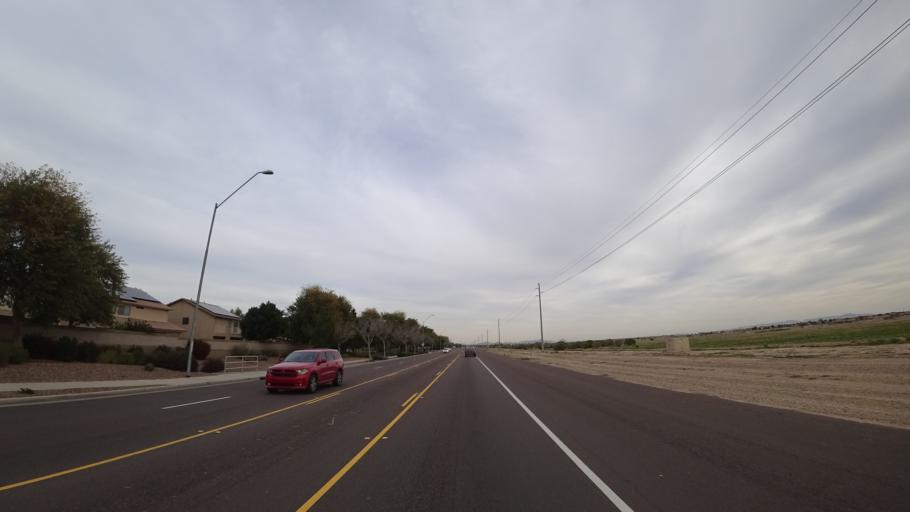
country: US
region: Arizona
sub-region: Maricopa County
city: Surprise
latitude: 33.6093
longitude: -112.3747
